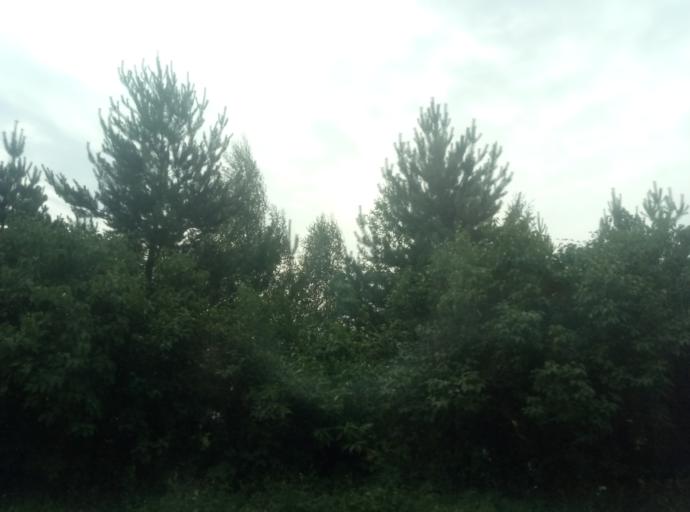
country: RU
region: Tula
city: Bogoroditsk
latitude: 53.7727
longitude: 38.1483
